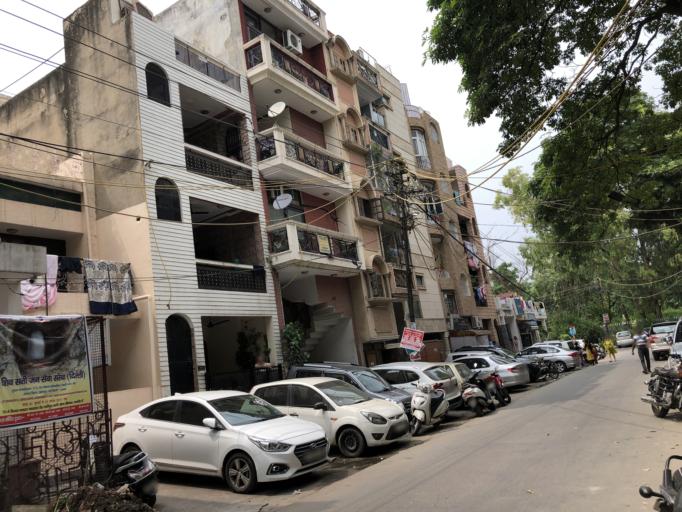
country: IN
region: NCT
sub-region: New Delhi
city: New Delhi
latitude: 28.5782
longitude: 77.2432
